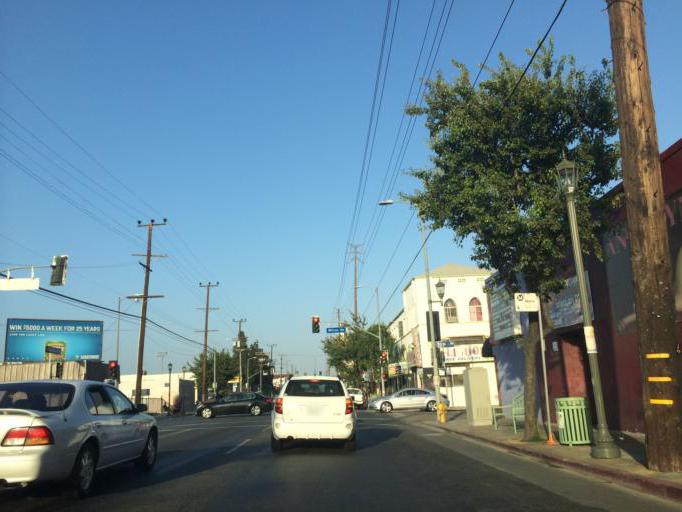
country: US
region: California
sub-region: Los Angeles County
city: Hollywood
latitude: 34.0907
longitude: -118.3314
